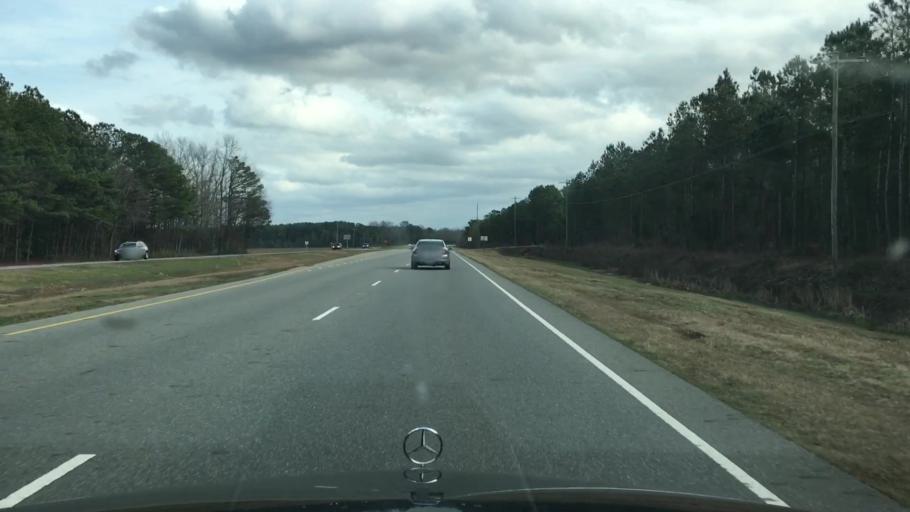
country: US
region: North Carolina
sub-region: Duplin County
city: Kenansville
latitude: 34.9497
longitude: -77.8881
